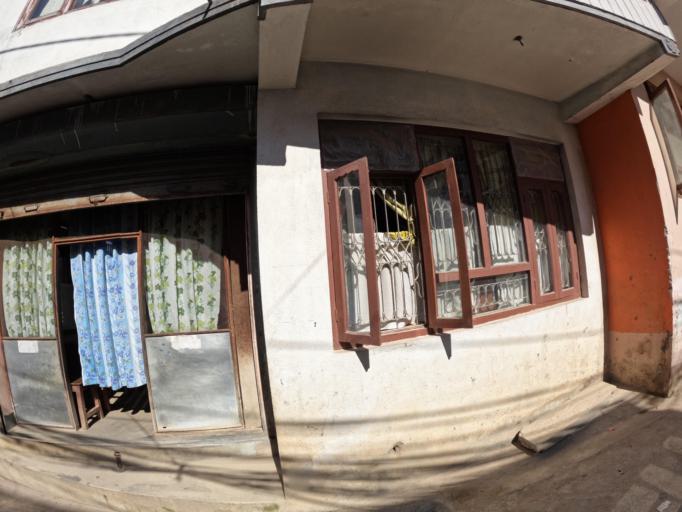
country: NP
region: Central Region
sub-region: Bagmati Zone
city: Kathmandu
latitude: 27.7487
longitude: 85.3359
